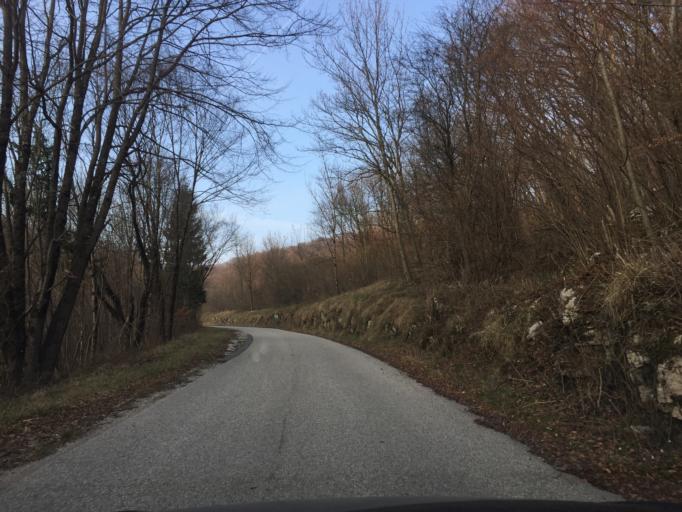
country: SI
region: Kanal
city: Kanal
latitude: 46.0583
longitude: 13.6670
